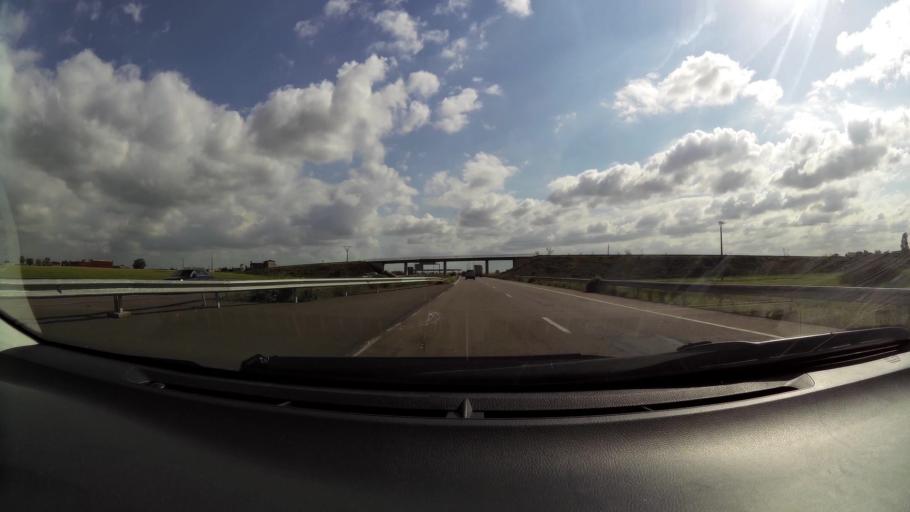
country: MA
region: Chaouia-Ouardigha
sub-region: Settat Province
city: Berrechid
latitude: 33.2382
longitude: -7.5699
